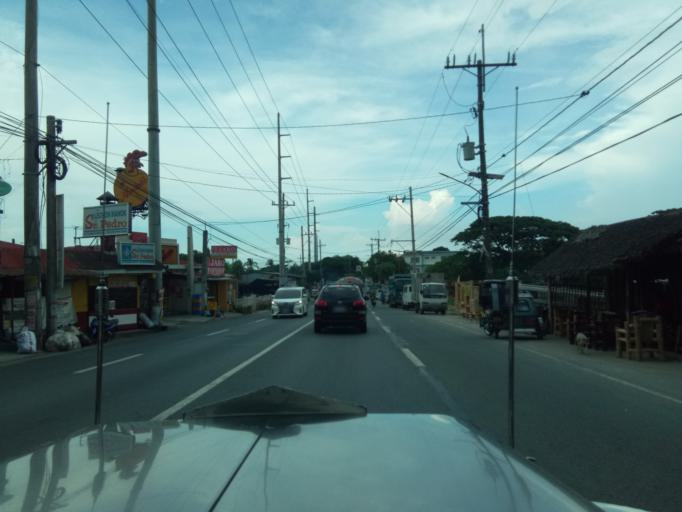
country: PH
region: Calabarzon
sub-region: Province of Cavite
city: Aliang
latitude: 14.2822
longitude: 120.8909
